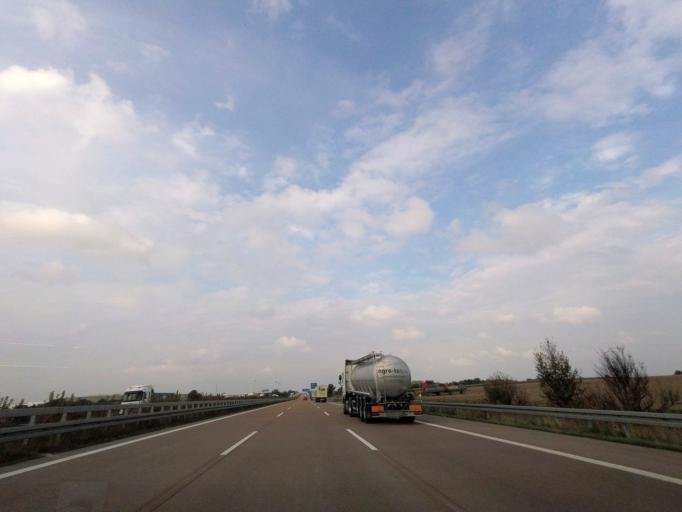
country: DE
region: Saxony-Anhalt
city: Osterfeld
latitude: 51.0768
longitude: 11.9556
